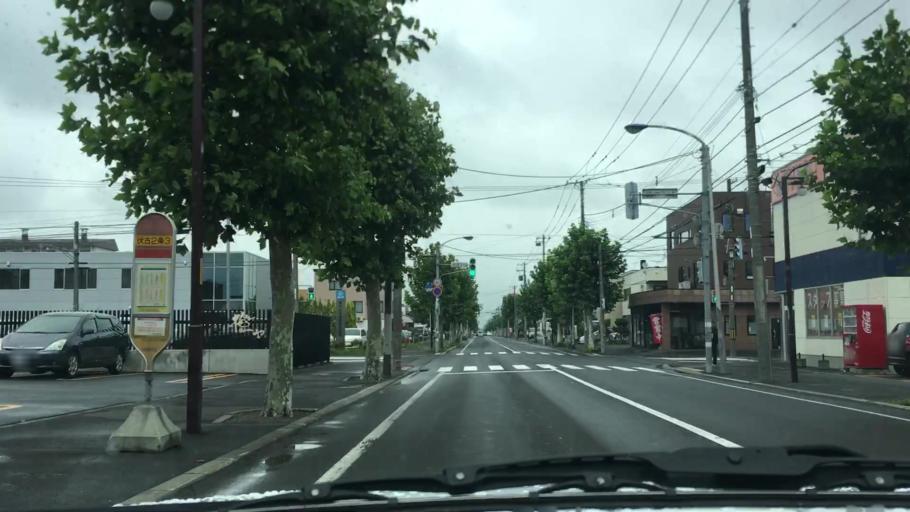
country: JP
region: Hokkaido
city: Sapporo
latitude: 43.0839
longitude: 141.3906
